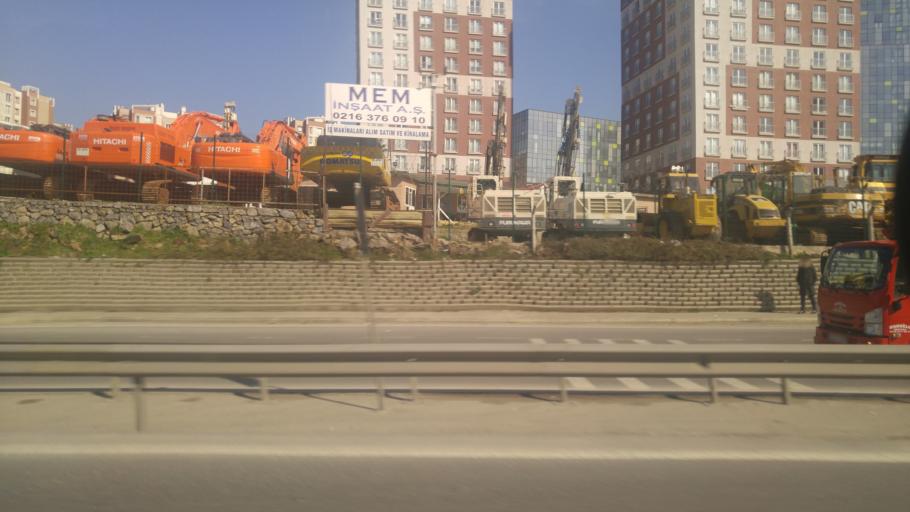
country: TR
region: Istanbul
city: Maltepe
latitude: 40.9113
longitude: 29.1968
